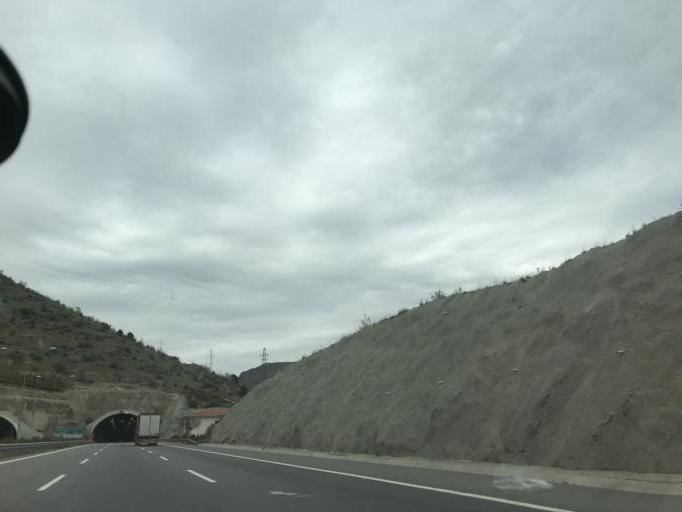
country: TR
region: Nigde
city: Ciftehan
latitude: 37.5731
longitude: 34.7533
